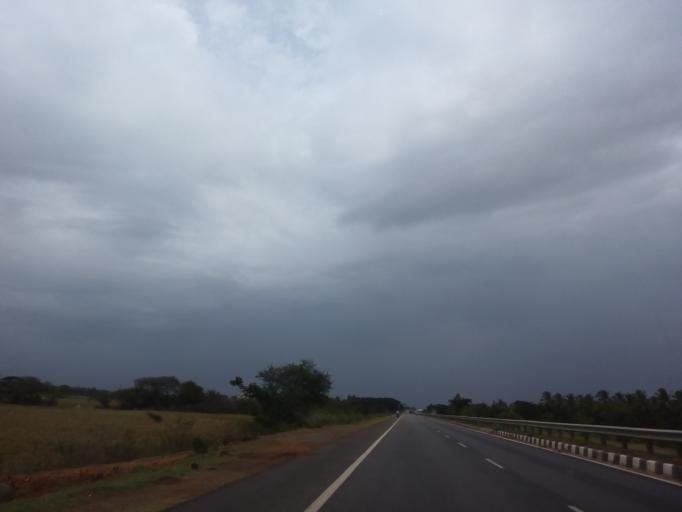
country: IN
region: Karnataka
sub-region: Davanagere
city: Harihar
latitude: 14.4731
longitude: 75.8280
